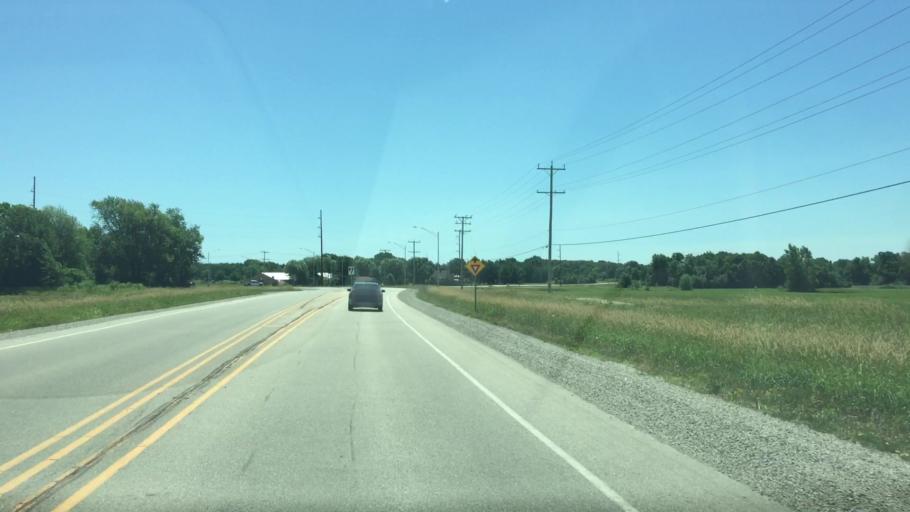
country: US
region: Wisconsin
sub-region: Outagamie County
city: Combined Locks
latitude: 44.2017
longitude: -88.3268
